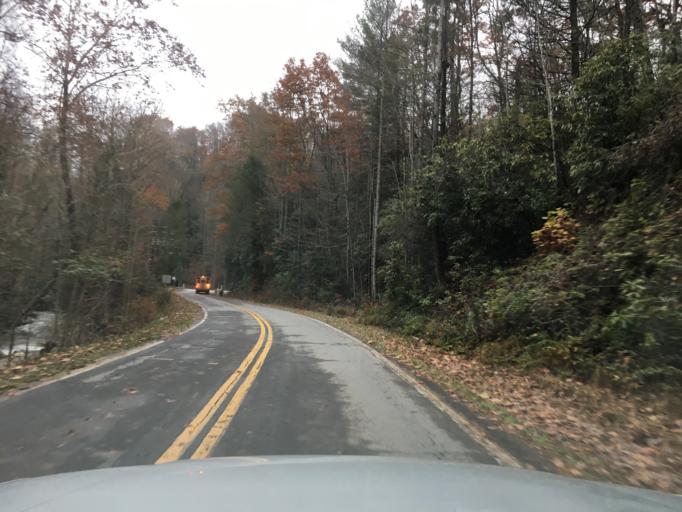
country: US
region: North Carolina
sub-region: Rutherford County
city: Lake Lure
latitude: 35.5241
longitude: -82.2474
